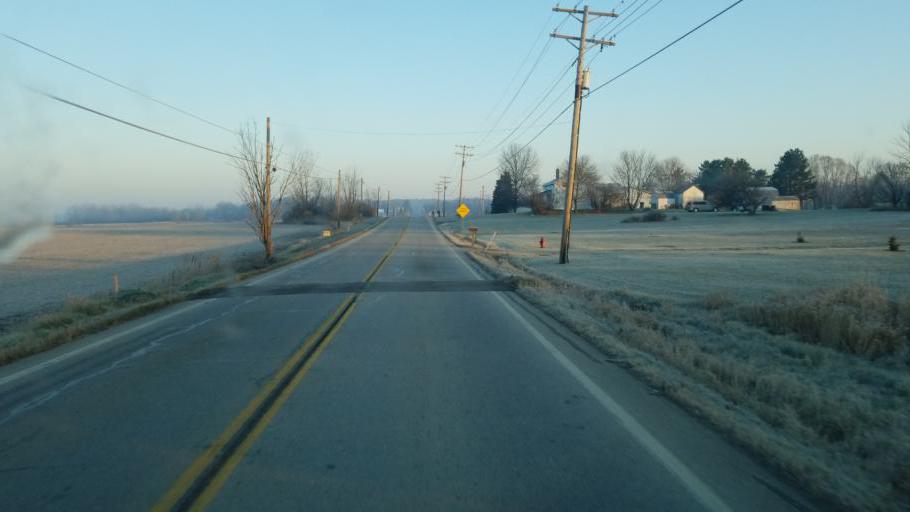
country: US
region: Ohio
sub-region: Medina County
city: Lodi
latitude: 41.0098
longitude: -81.9961
